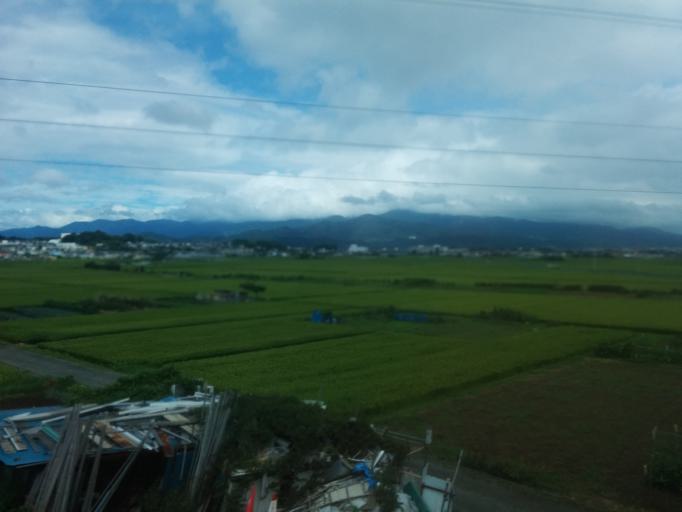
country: JP
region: Kanagawa
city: Hiratsuka
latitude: 35.3469
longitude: 139.3117
